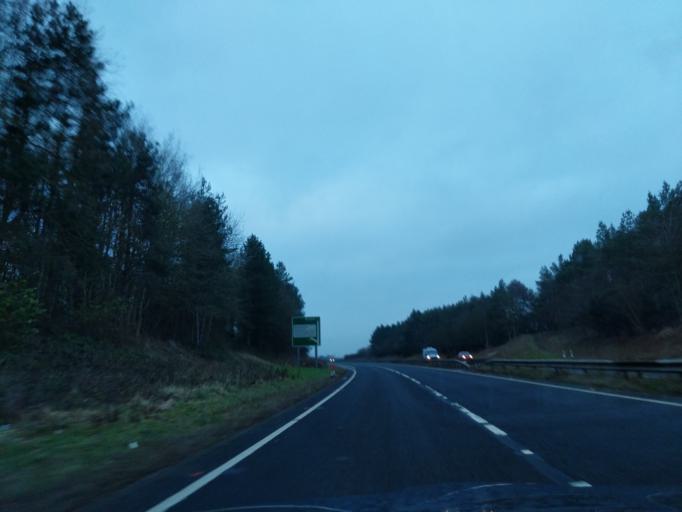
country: GB
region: England
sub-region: Northumberland
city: Stannington
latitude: 55.1087
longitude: -1.6638
